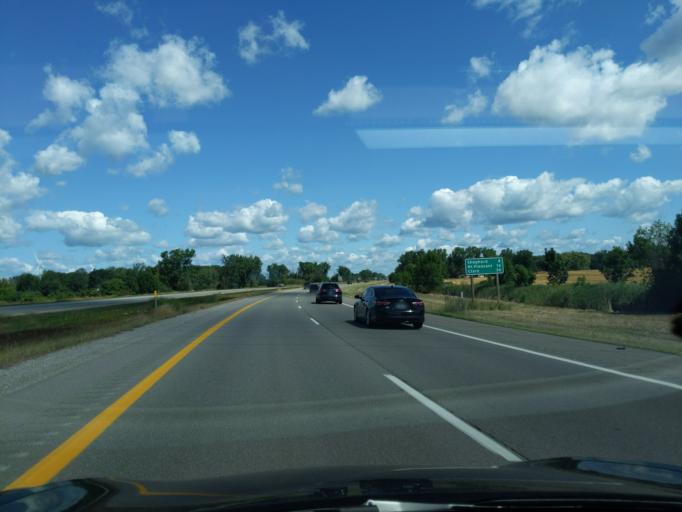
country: US
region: Michigan
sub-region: Gratiot County
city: Alma
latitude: 43.4188
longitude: -84.6766
